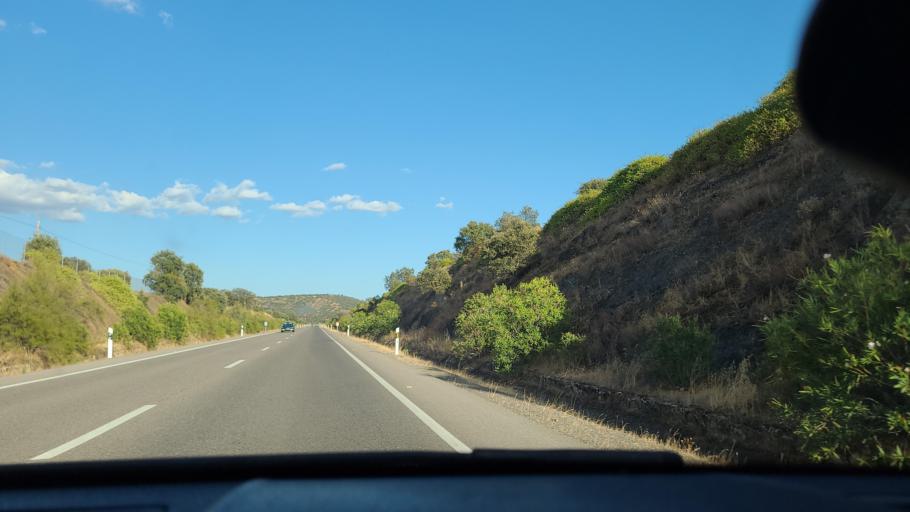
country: ES
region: Andalusia
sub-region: Province of Cordoba
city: Belmez
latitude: 38.2049
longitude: -5.1192
